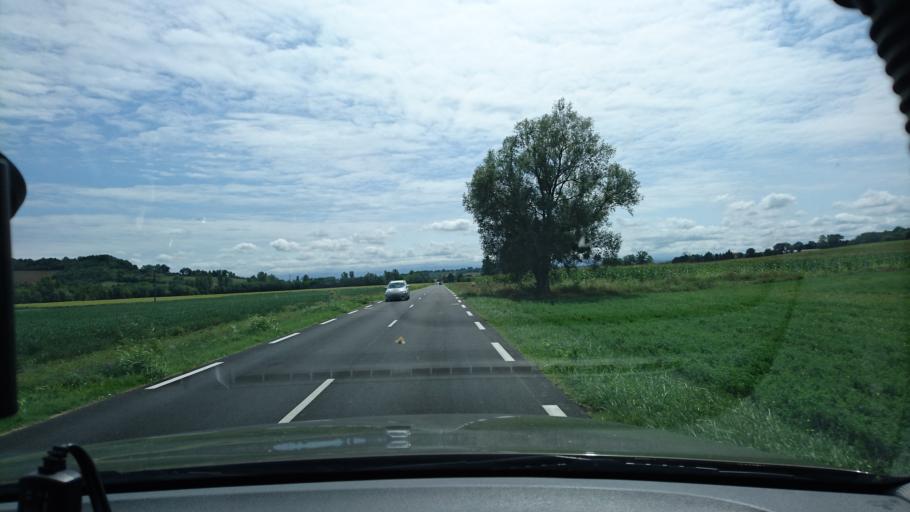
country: FR
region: Midi-Pyrenees
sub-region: Departement de l'Ariege
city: Lezat-sur-Leze
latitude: 43.2210
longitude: 1.3803
